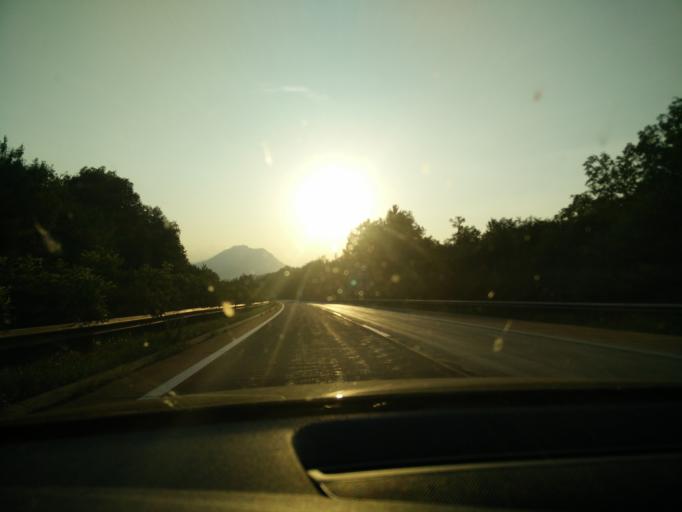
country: AT
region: Carinthia
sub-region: Politischer Bezirk Villach Land
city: Wernberg
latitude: 46.6236
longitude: 13.9293
